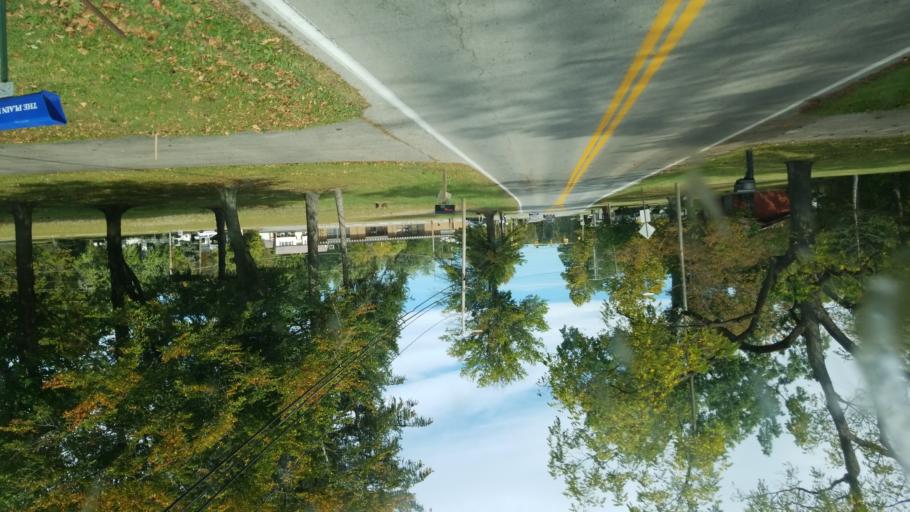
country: US
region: Ohio
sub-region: Lorain County
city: Amherst
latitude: 41.4172
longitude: -82.2237
